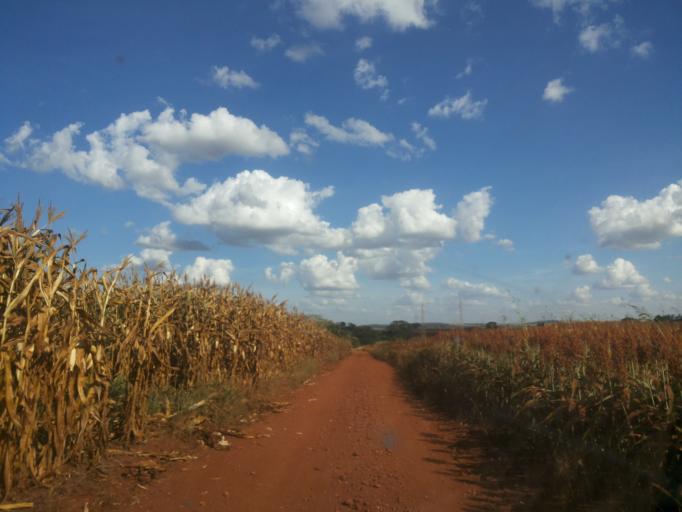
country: BR
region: Minas Gerais
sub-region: Capinopolis
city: Capinopolis
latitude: -18.5903
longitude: -49.4952
